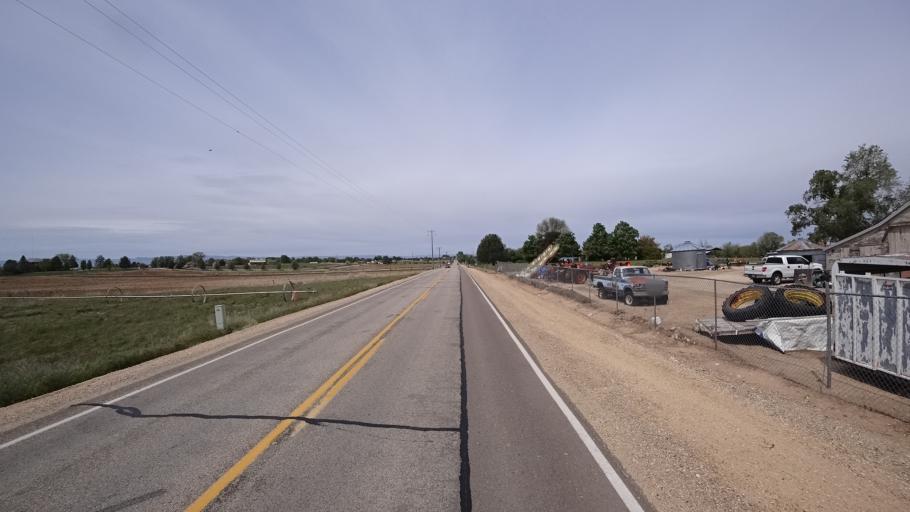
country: US
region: Idaho
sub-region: Ada County
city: Meridian
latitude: 43.5609
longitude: -116.4011
